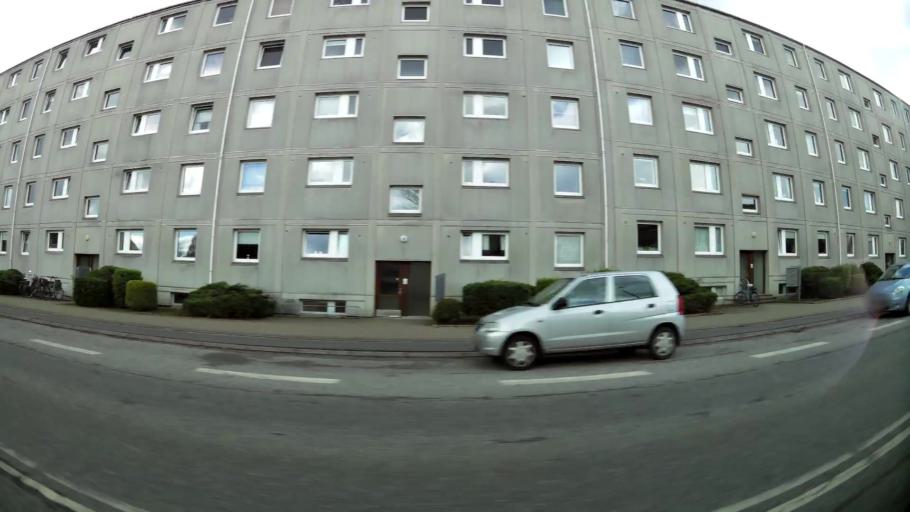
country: DK
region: South Denmark
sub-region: Fredericia Kommune
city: Fredericia
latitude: 55.5679
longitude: 9.7428
